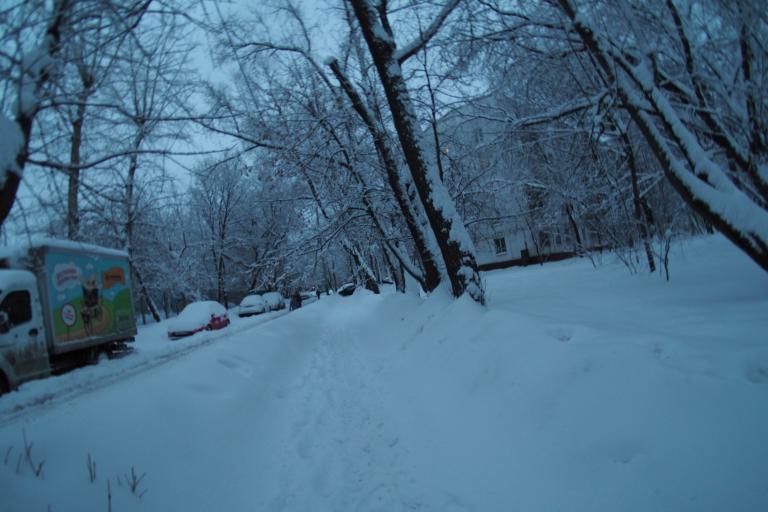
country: RU
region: Moscow
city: Perovo
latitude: 55.7427
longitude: 37.7797
